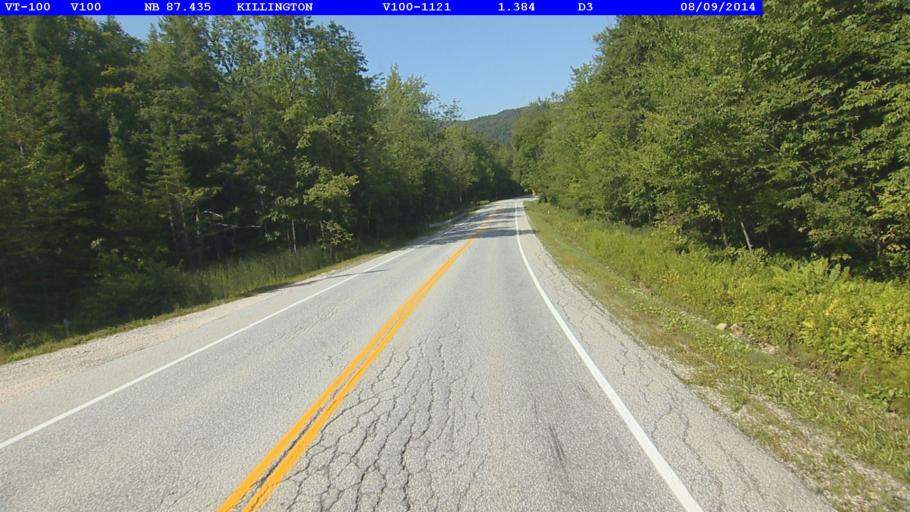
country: US
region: Vermont
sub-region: Rutland County
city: Rutland
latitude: 43.6859
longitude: -72.8136
